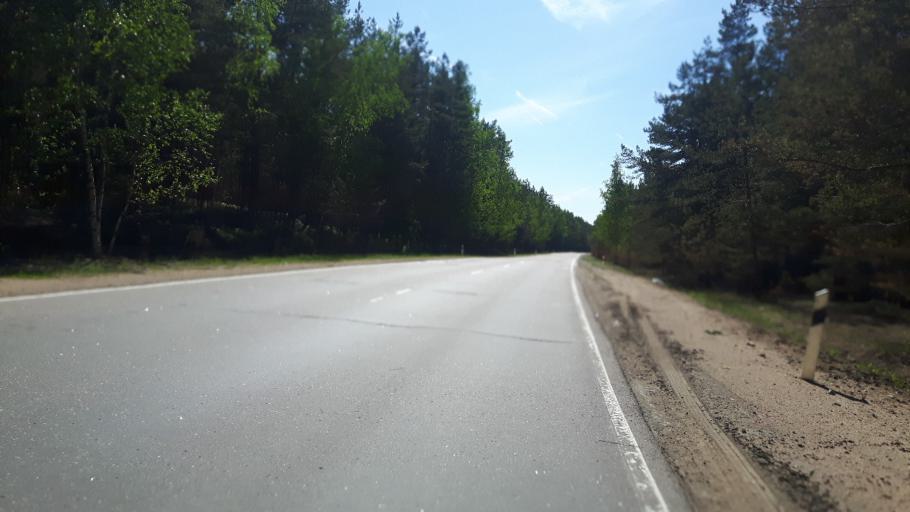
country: RU
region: Leningrad
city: Sista-Palkino
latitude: 59.7767
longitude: 28.8620
